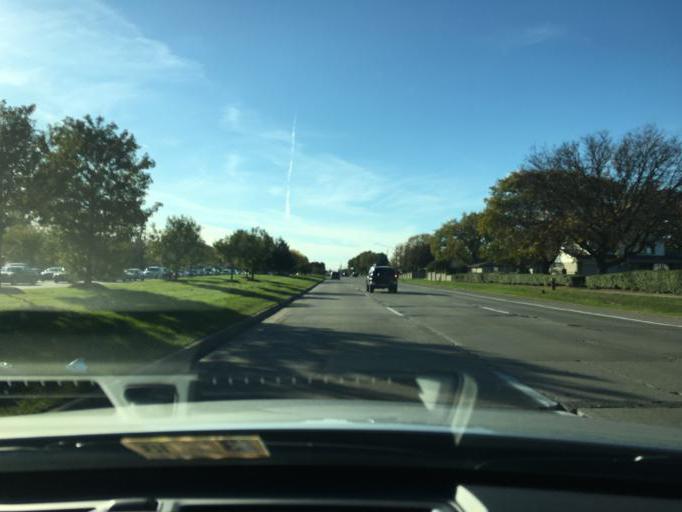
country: US
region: Michigan
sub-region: Macomb County
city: Sterling Heights
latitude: 42.5663
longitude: -83.0170
